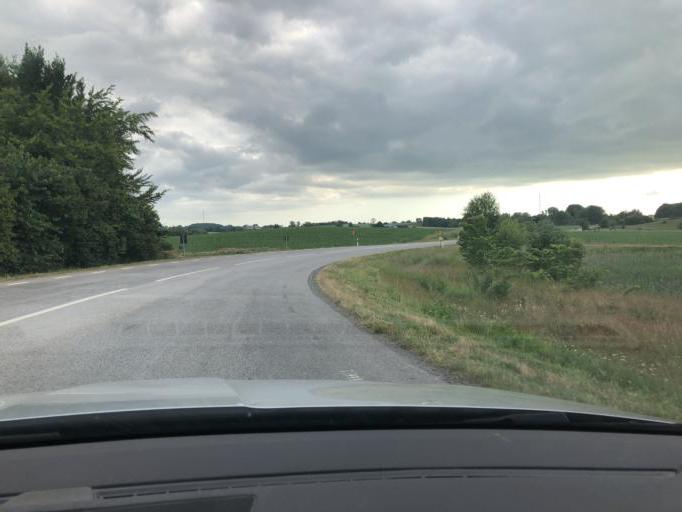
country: SE
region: Skane
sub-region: Simrishamns Kommun
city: Simrishamn
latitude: 55.5348
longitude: 14.2756
